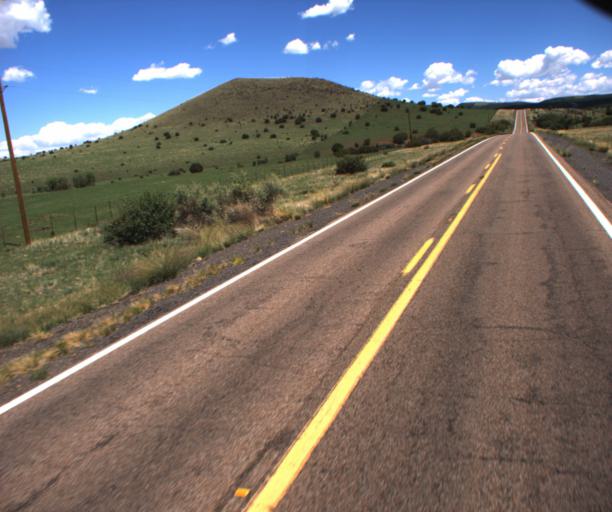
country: US
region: Arizona
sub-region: Navajo County
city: Pinetop-Lakeside
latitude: 34.2709
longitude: -109.6548
